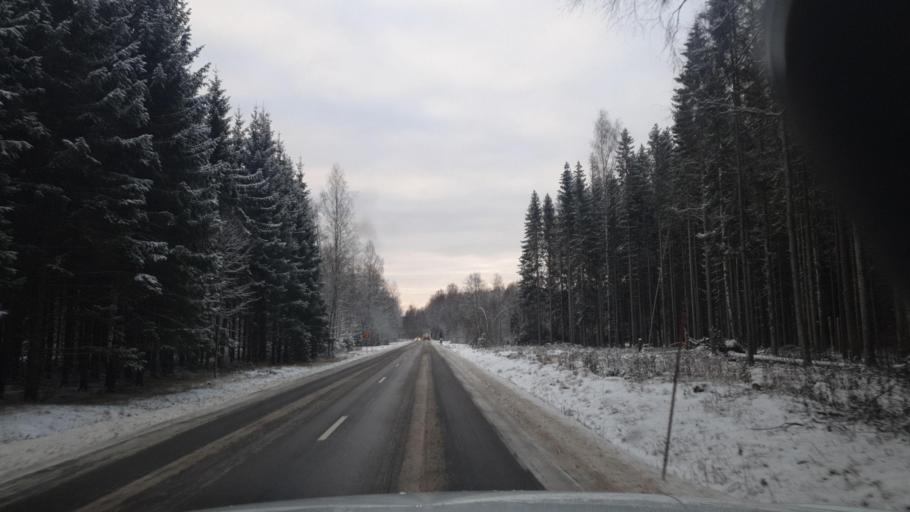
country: SE
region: Vaermland
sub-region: Eda Kommun
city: Charlottenberg
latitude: 59.8310
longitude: 12.2648
